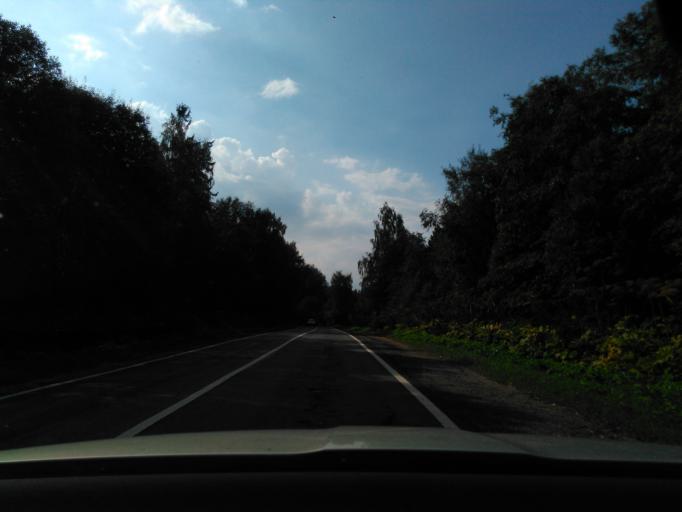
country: RU
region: Moskovskaya
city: Solnechnogorsk
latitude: 56.1422
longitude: 36.8345
